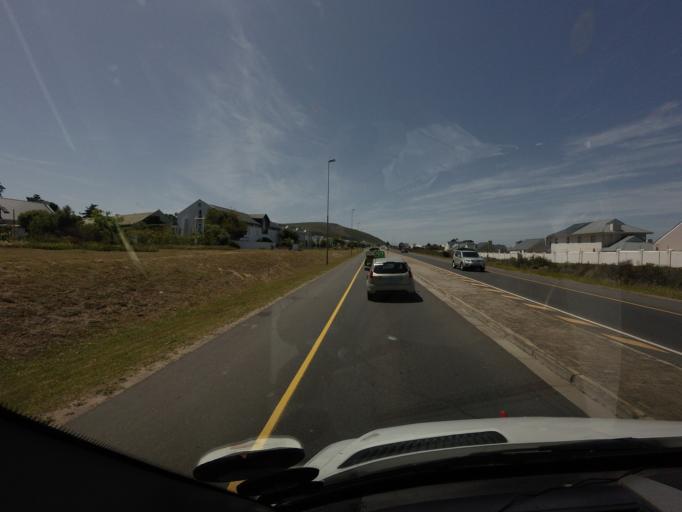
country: ZA
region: Western Cape
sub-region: Overberg District Municipality
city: Hermanus
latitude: -34.4115
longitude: 19.1979
